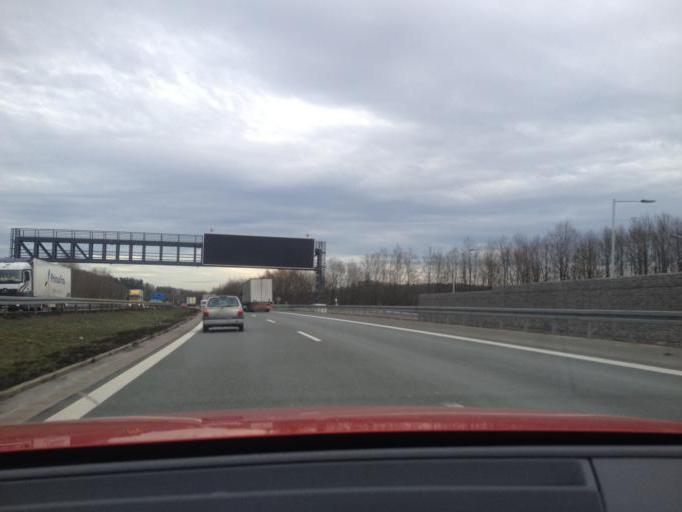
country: DE
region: Bavaria
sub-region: Regierungsbezirk Mittelfranken
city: Schnelldorf
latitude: 49.2045
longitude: 10.1989
